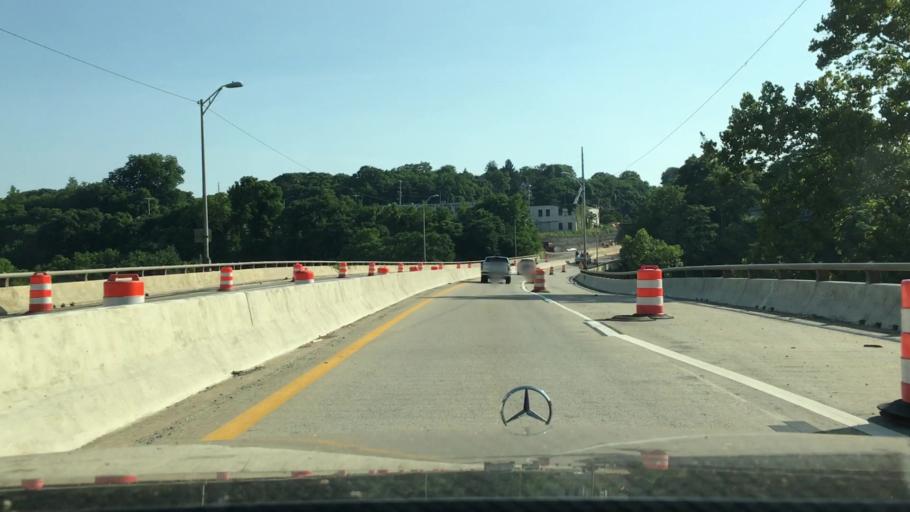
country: US
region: Virginia
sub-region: City of Lynchburg
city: Lynchburg
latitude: 37.4104
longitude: -79.1341
